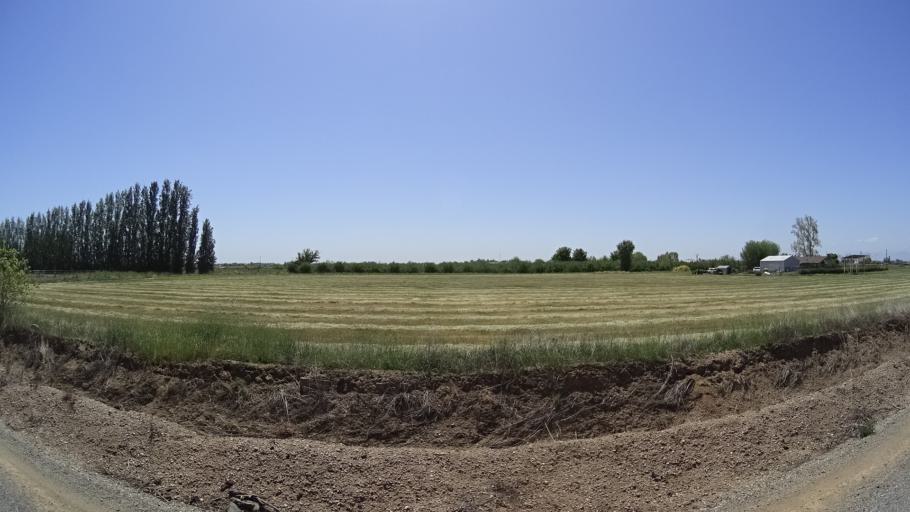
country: US
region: California
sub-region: Glenn County
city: Orland
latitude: 39.7796
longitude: -122.1488
